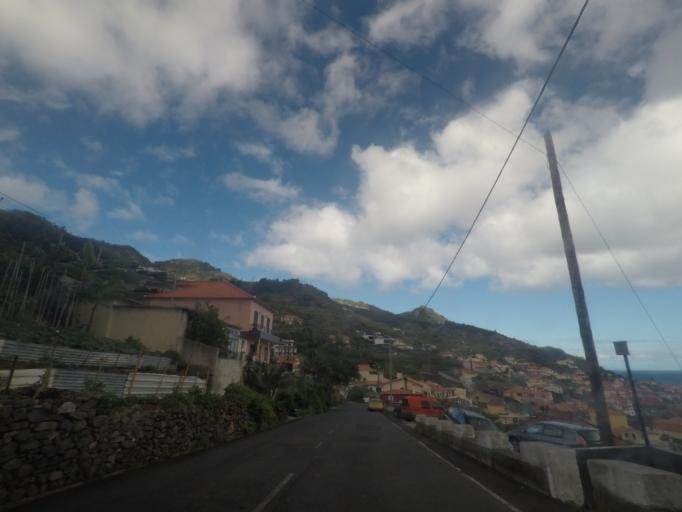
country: PT
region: Madeira
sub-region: Machico
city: Machico
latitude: 32.7305
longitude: -16.7732
